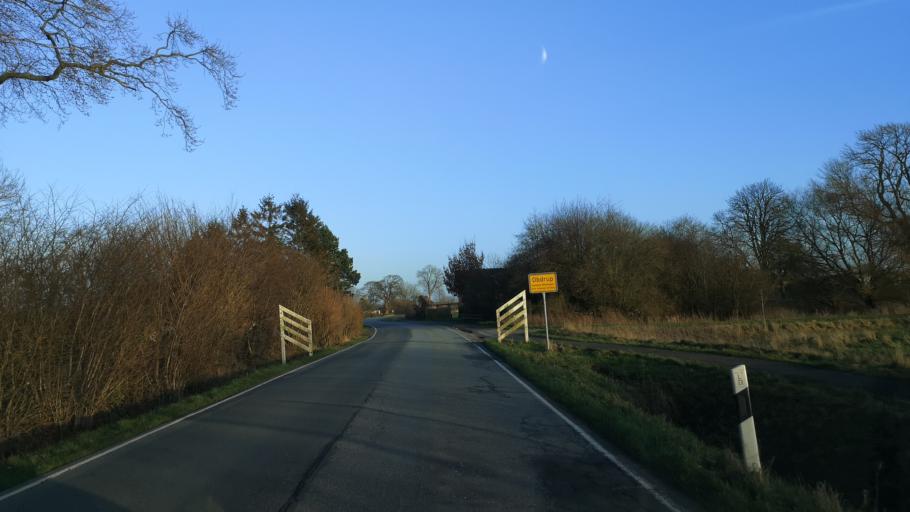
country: DE
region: Schleswig-Holstein
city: Ausacker
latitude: 54.6965
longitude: 9.5630
